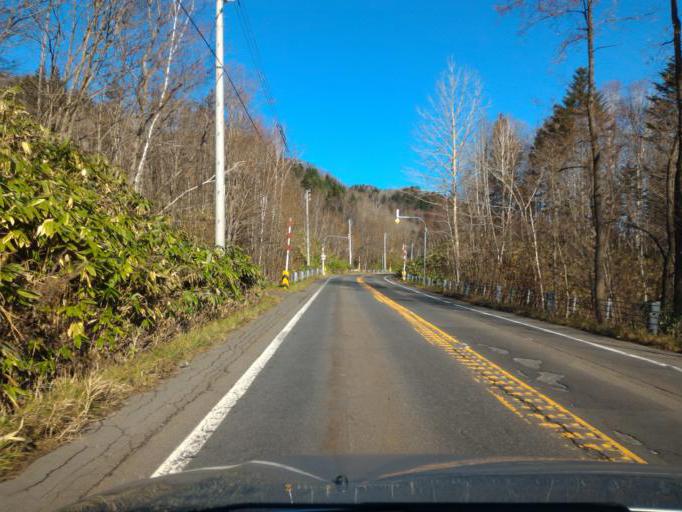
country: JP
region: Hokkaido
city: Bibai
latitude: 43.2648
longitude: 142.0319
